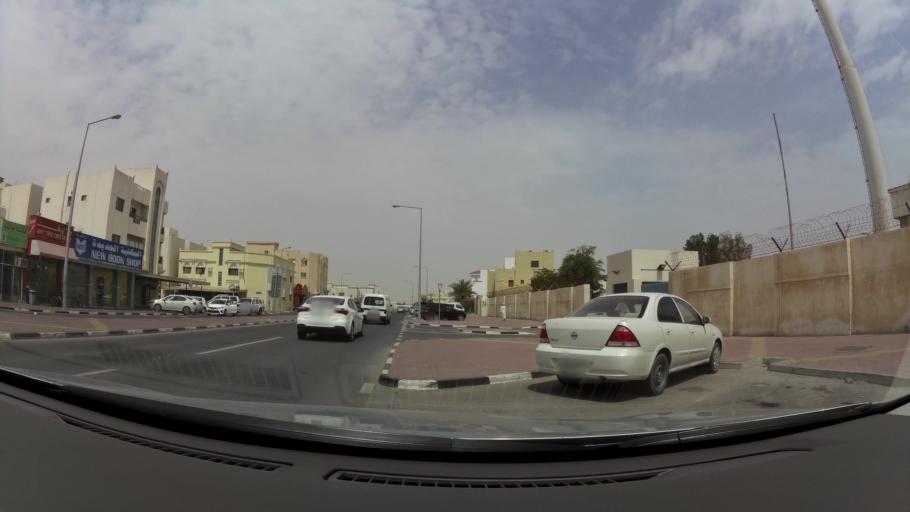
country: QA
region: Baladiyat ad Dawhah
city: Doha
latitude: 25.3168
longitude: 51.4780
